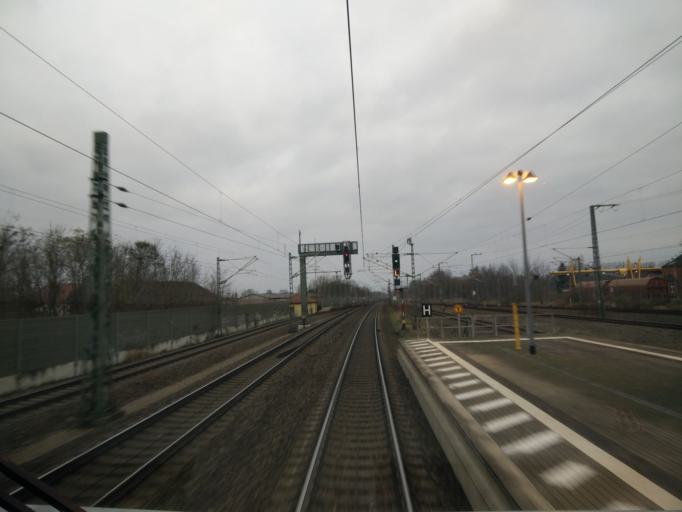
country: DE
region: Brandenburg
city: Wittenberge
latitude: 53.0063
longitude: 11.7621
